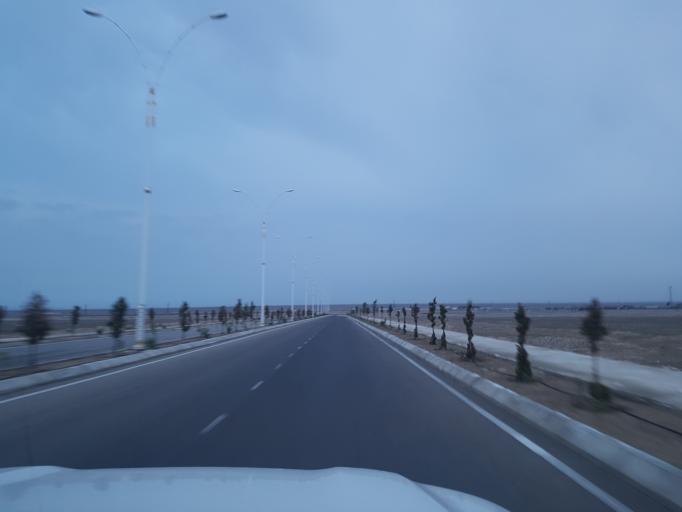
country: TM
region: Balkan
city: Balkanabat
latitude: 39.5562
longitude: 54.2947
